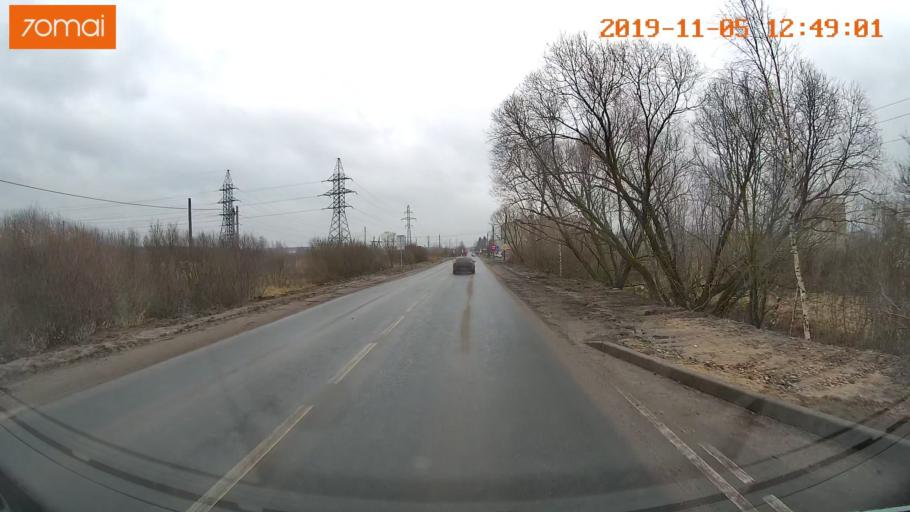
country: RU
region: Ivanovo
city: Kokhma
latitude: 56.9574
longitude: 41.1018
